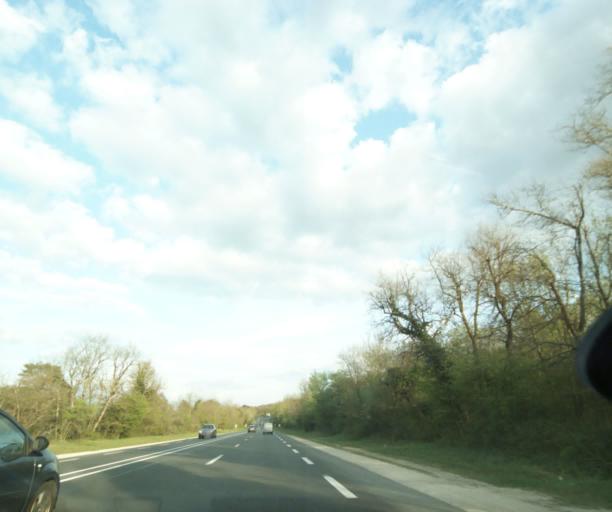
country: FR
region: Ile-de-France
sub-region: Departement de Seine-et-Marne
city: Barbizon
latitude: 48.4435
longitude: 2.6436
